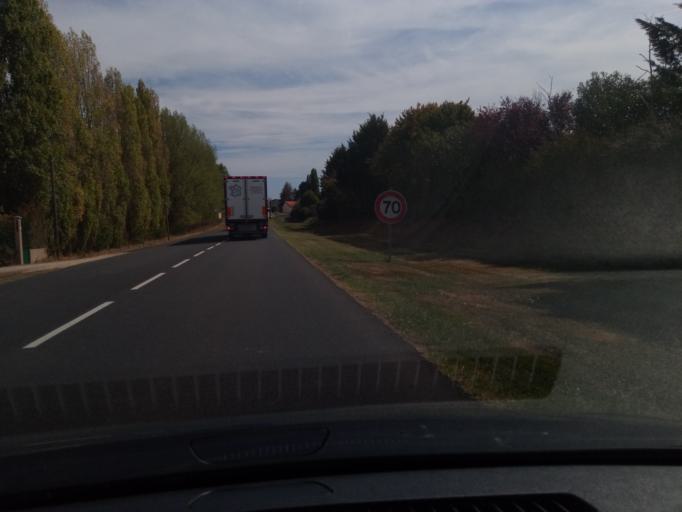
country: FR
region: Poitou-Charentes
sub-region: Departement de la Vienne
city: Terce
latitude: 46.4811
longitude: 0.5156
